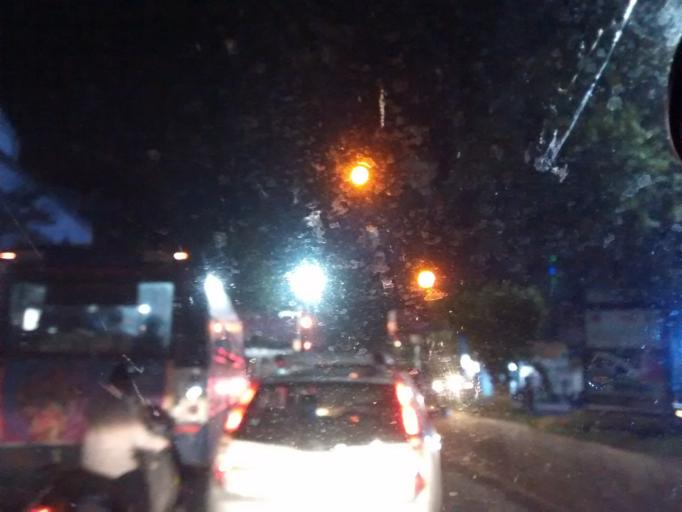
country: IN
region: Telangana
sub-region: Hyderabad
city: Malkajgiri
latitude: 17.4307
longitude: 78.4923
